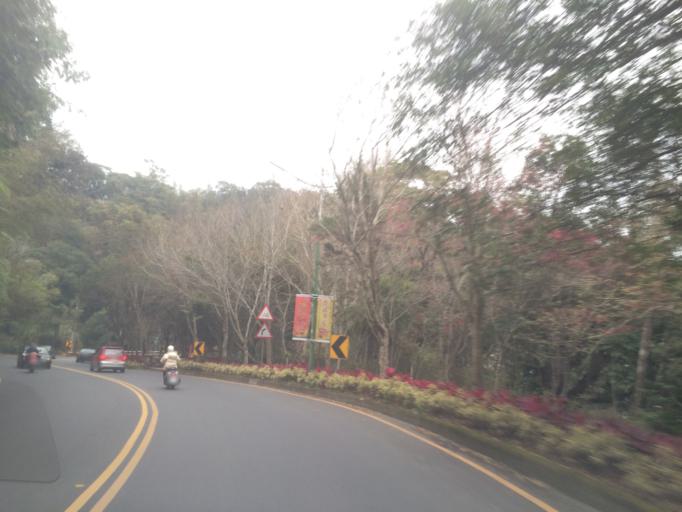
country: TW
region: Taiwan
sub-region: Nantou
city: Puli
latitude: 23.8707
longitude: 120.9165
